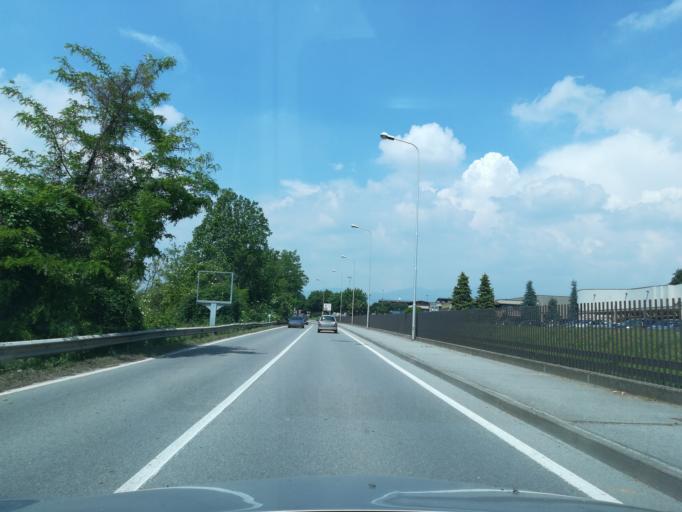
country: IT
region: Lombardy
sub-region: Provincia di Bergamo
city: Grassobbio
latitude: 45.6637
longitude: 9.7423
